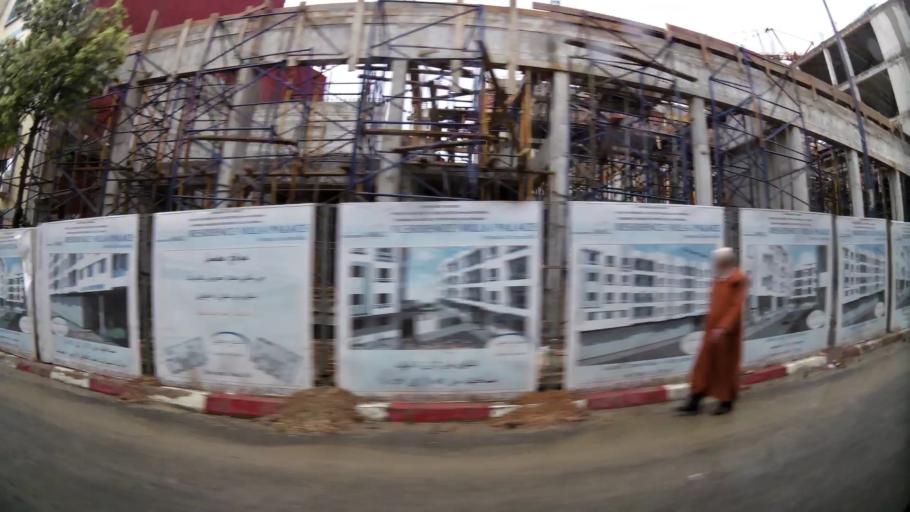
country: MA
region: Taza-Al Hoceima-Taounate
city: Al Hoceima
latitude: 35.2529
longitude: -3.9345
